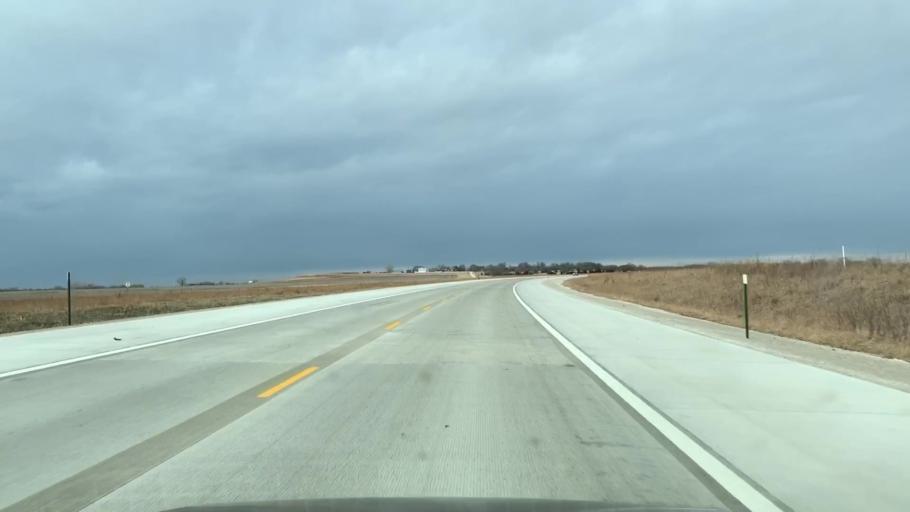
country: US
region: Kansas
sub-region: Allen County
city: Humboldt
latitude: 37.8505
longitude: -95.4098
